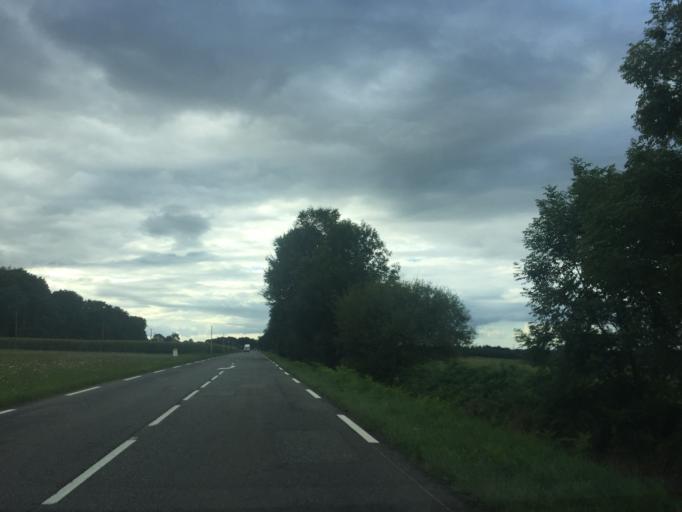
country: FR
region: Midi-Pyrenees
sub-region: Departement des Hautes-Pyrenees
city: Capvern
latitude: 43.0844
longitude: 0.3451
